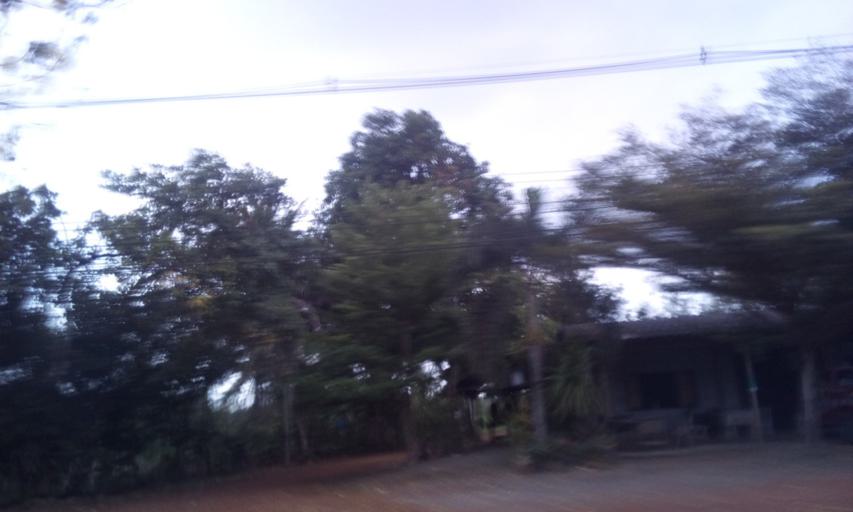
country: TH
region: Chanthaburi
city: Khlung
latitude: 12.4456
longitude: 102.2929
